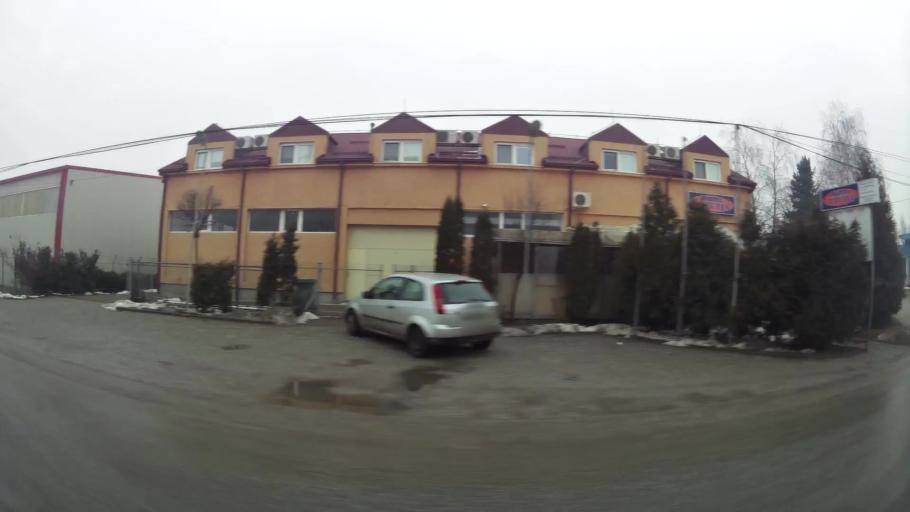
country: MK
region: Petrovec
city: Petrovec
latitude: 41.9429
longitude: 21.6054
